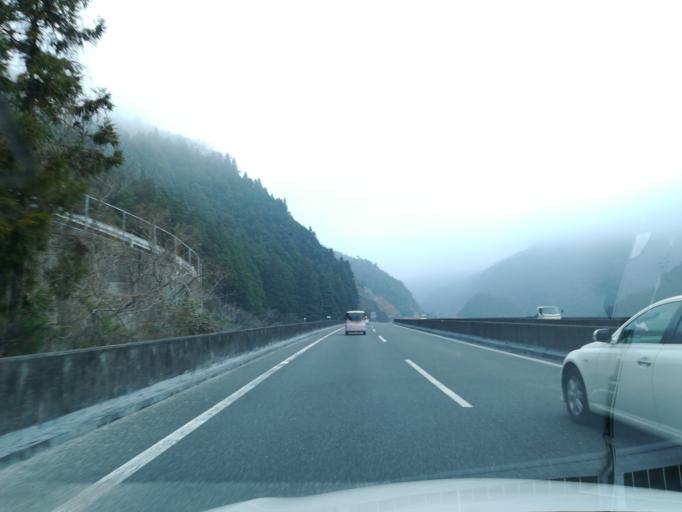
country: JP
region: Ehime
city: Kawanoecho
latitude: 33.7823
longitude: 133.6616
